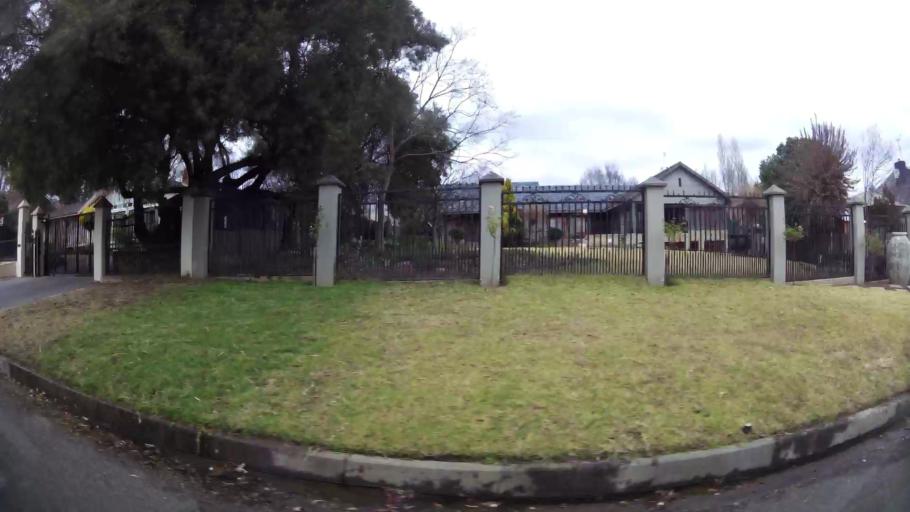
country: ZA
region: Orange Free State
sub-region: Fezile Dabi District Municipality
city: Kroonstad
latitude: -27.6685
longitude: 27.2489
